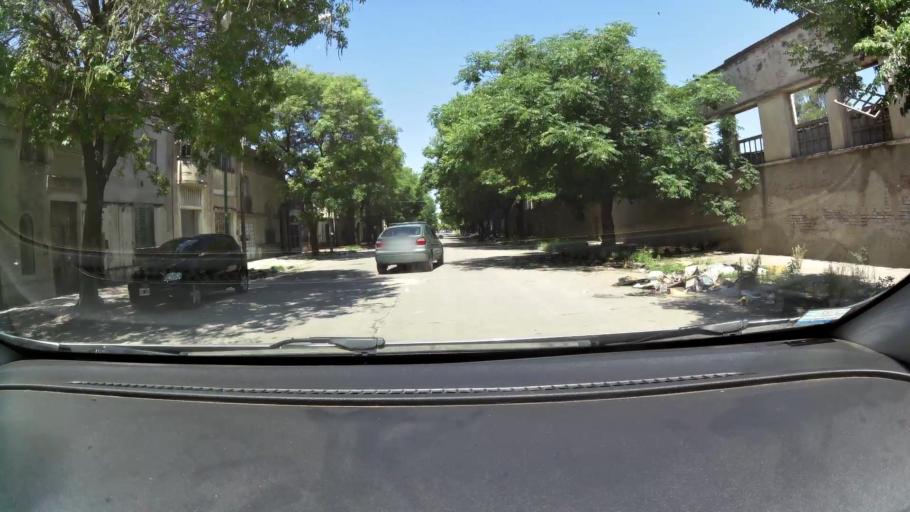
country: AR
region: Cordoba
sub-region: Departamento de Capital
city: Cordoba
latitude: -31.3905
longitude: -64.1904
